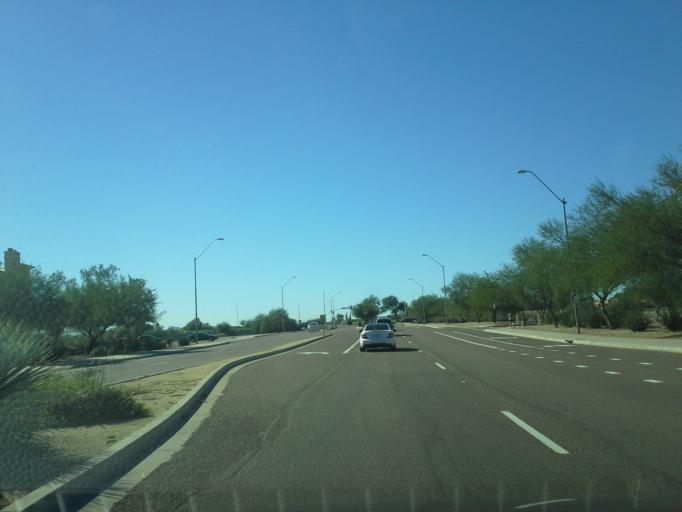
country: US
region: Arizona
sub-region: Maricopa County
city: Paradise Valley
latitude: 33.6402
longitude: -111.9044
